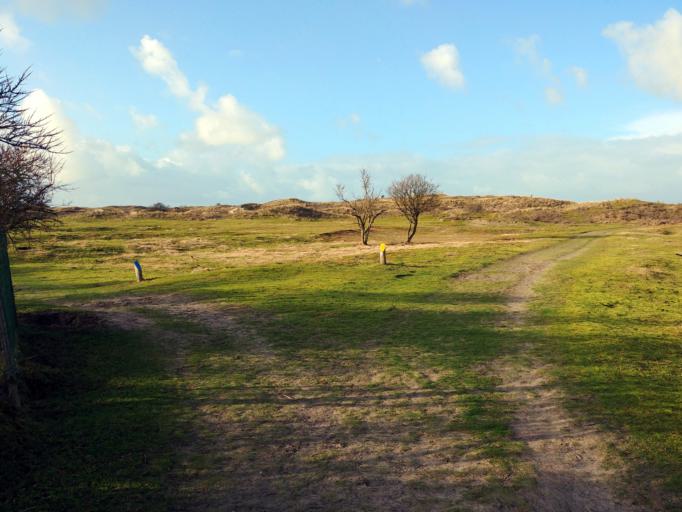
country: NL
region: South Holland
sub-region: Gemeente Noordwijkerhout
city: Noordwijkerhout
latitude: 52.2986
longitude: 4.5086
